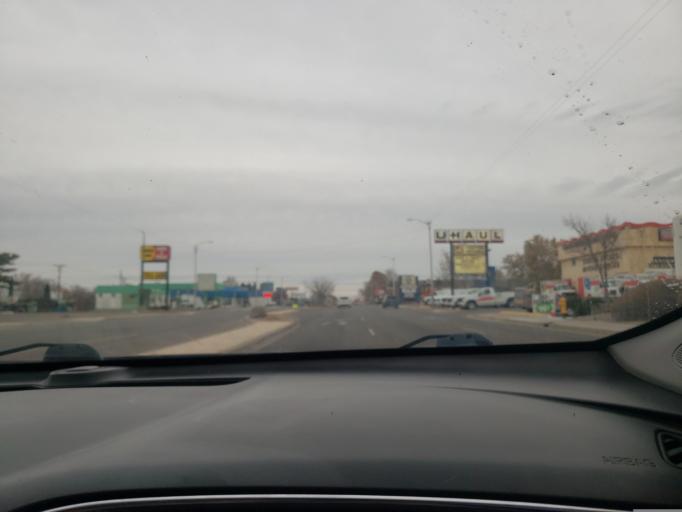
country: US
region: New Mexico
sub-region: Bernalillo County
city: North Valley
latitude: 35.1266
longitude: -106.5864
